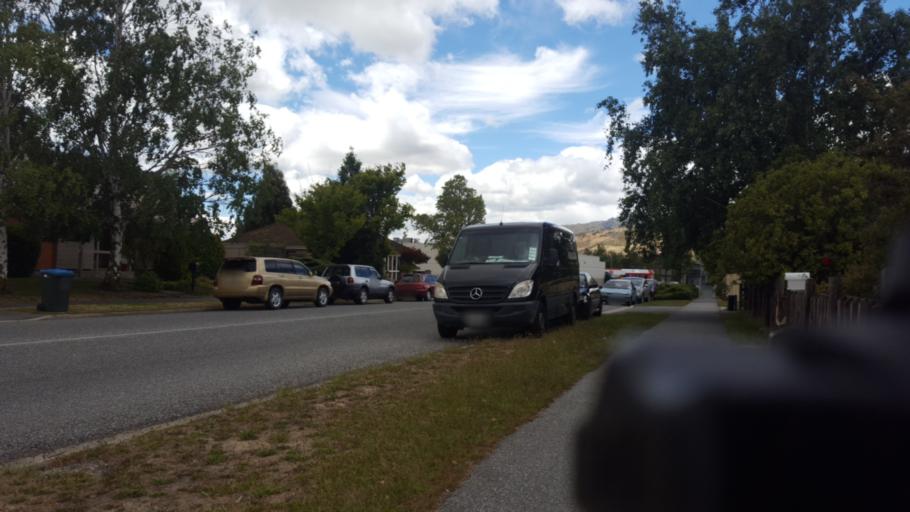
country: NZ
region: Otago
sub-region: Queenstown-Lakes District
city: Wanaka
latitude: -45.0384
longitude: 169.1929
